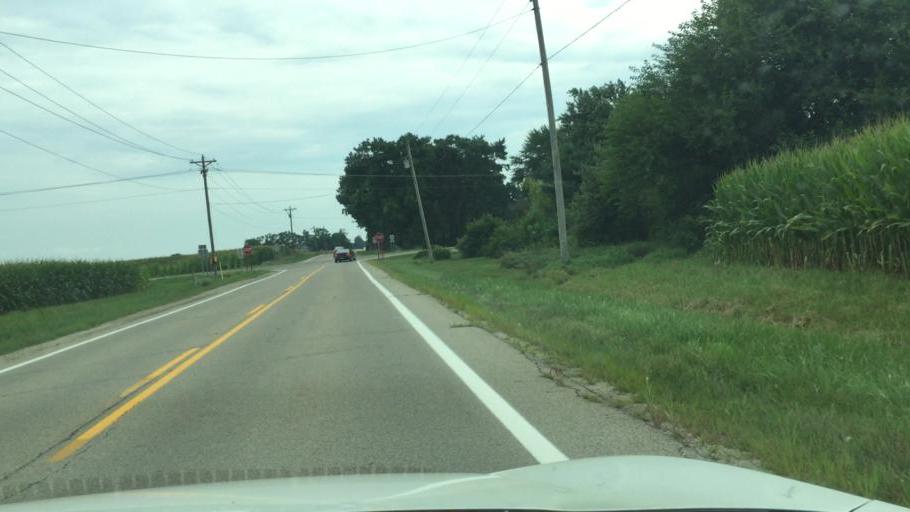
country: US
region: Ohio
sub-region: Champaign County
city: Mechanicsburg
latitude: 40.1434
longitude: -83.5295
